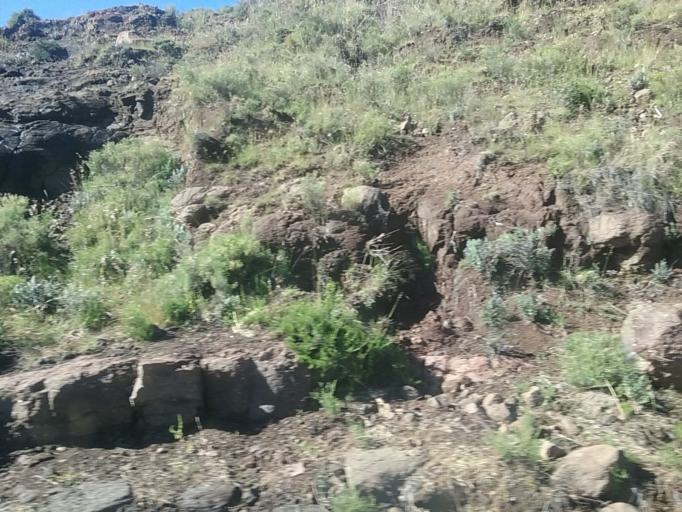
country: LS
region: Berea
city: Teyateyaneng
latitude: -29.2355
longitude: 27.9153
